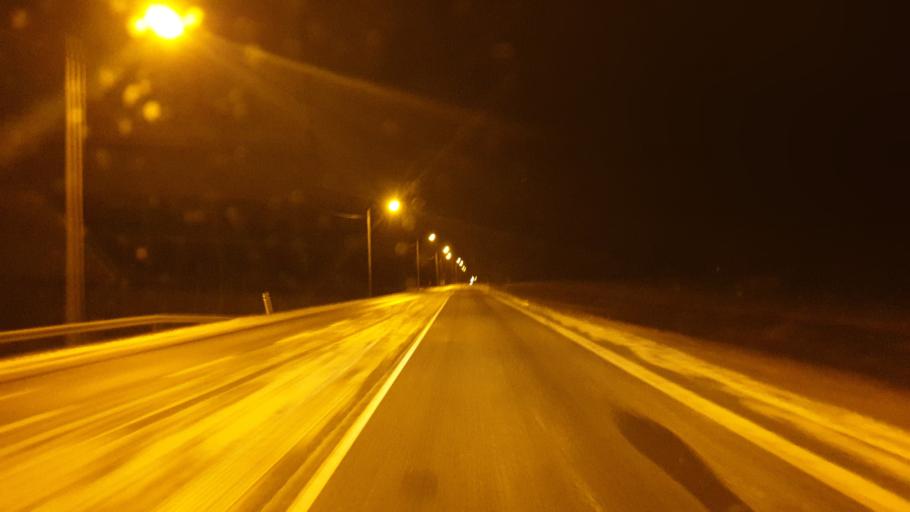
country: FI
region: Central Finland
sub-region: AEaenekoski
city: AEaenekoski
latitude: 62.7461
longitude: 25.7736
